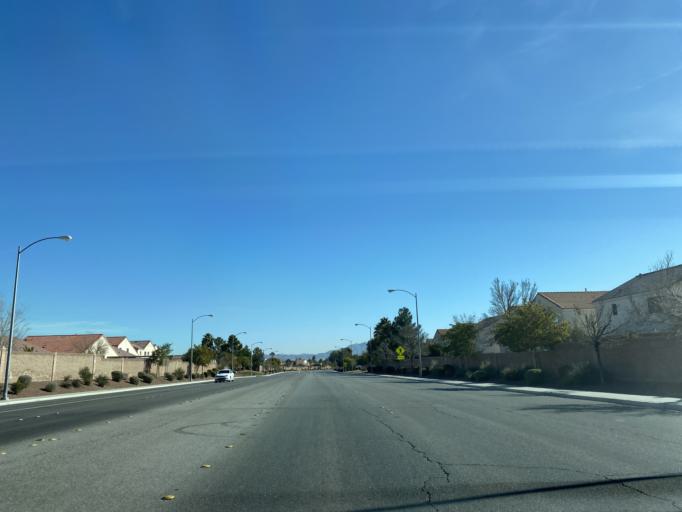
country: US
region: Nevada
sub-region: Clark County
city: North Las Vegas
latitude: 36.2830
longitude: -115.1490
